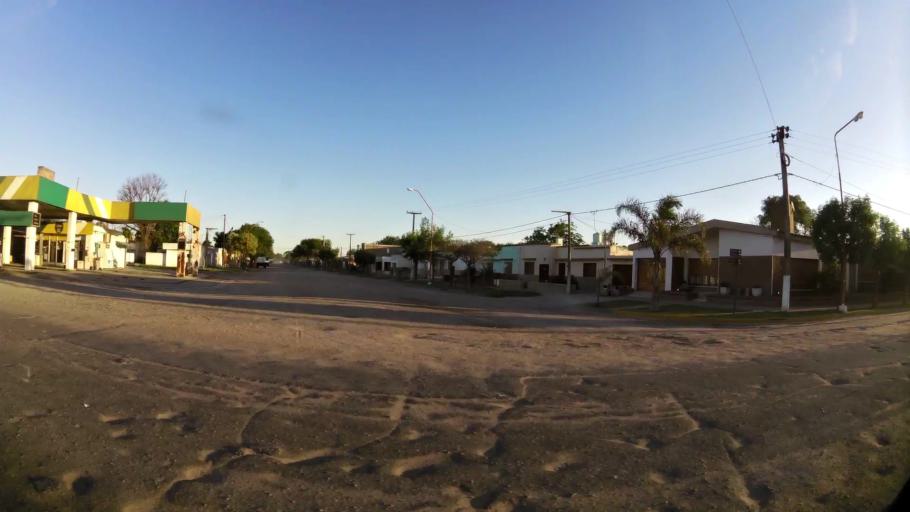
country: AR
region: Cordoba
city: La Playosa
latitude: -32.1018
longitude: -63.0338
